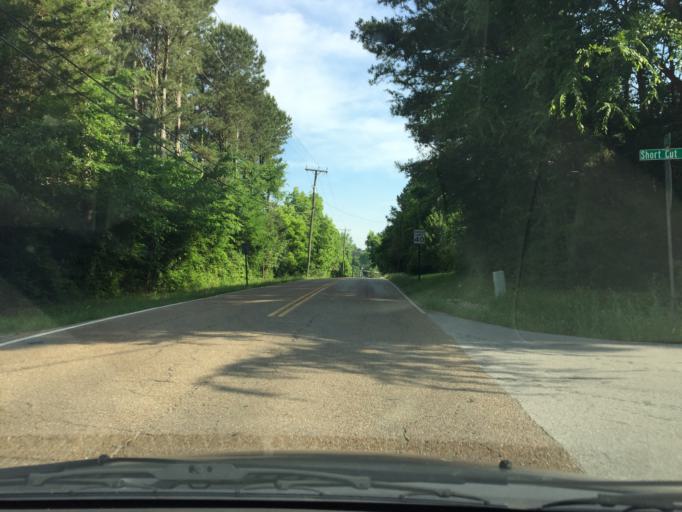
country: US
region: Tennessee
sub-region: Hamilton County
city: Apison
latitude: 35.0340
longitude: -85.0252
